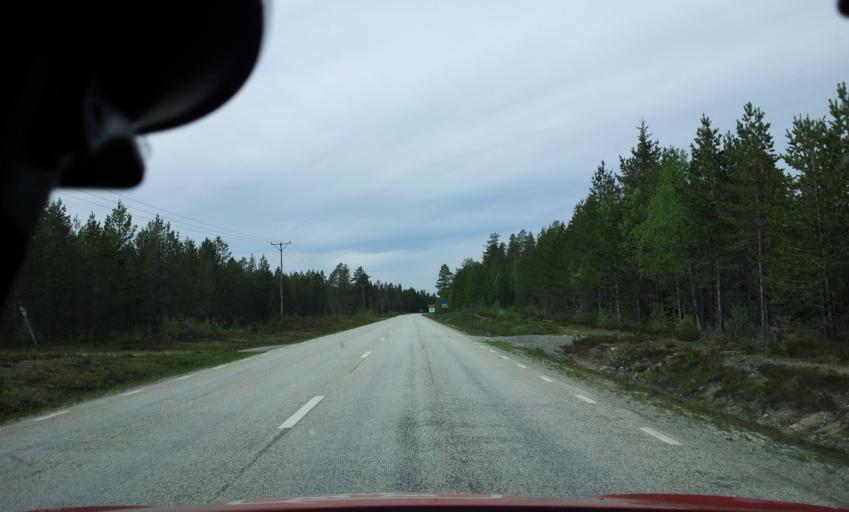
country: SE
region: Jaemtland
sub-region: Bergs Kommun
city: Hoverberg
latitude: 62.4999
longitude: 14.2062
